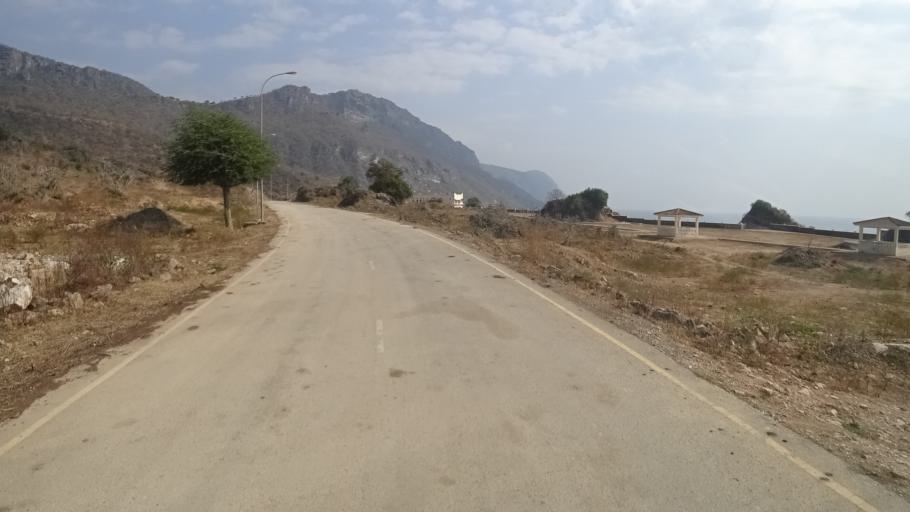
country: YE
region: Al Mahrah
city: Hawf
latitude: 16.7082
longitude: 53.2605
